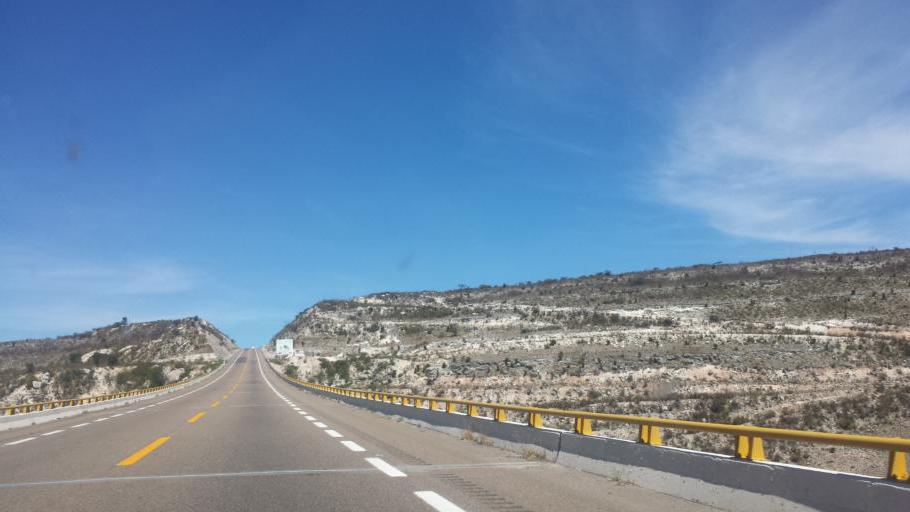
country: MX
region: Oaxaca
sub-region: Villa Tejupam de la Union
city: Villa Tejupam de la Union
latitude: 17.9086
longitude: -97.3645
